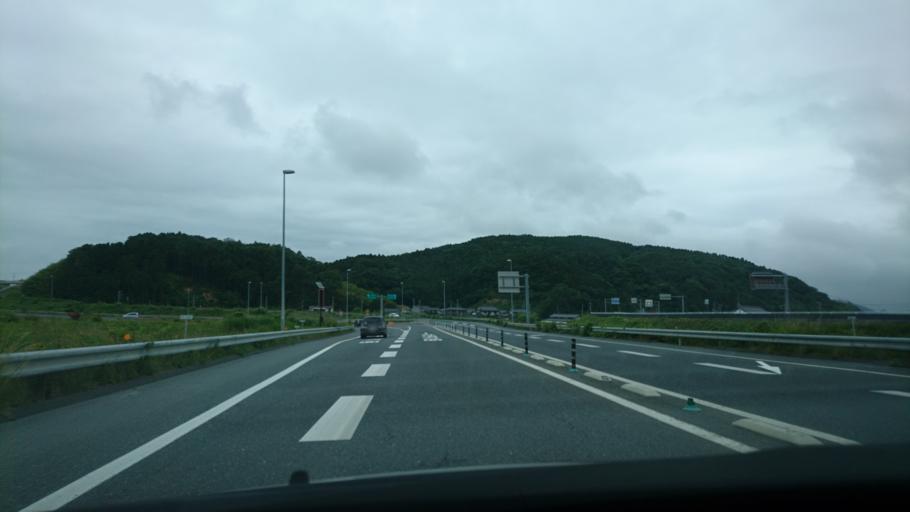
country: JP
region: Miyagi
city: Ishinomaki
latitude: 38.4972
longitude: 141.2882
